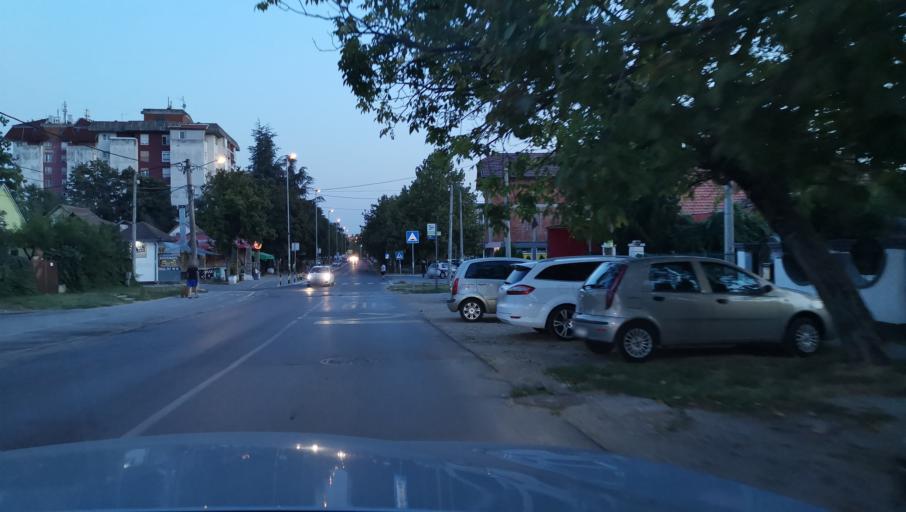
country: RS
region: Central Serbia
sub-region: Belgrade
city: Obrenovac
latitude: 44.6632
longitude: 20.2037
